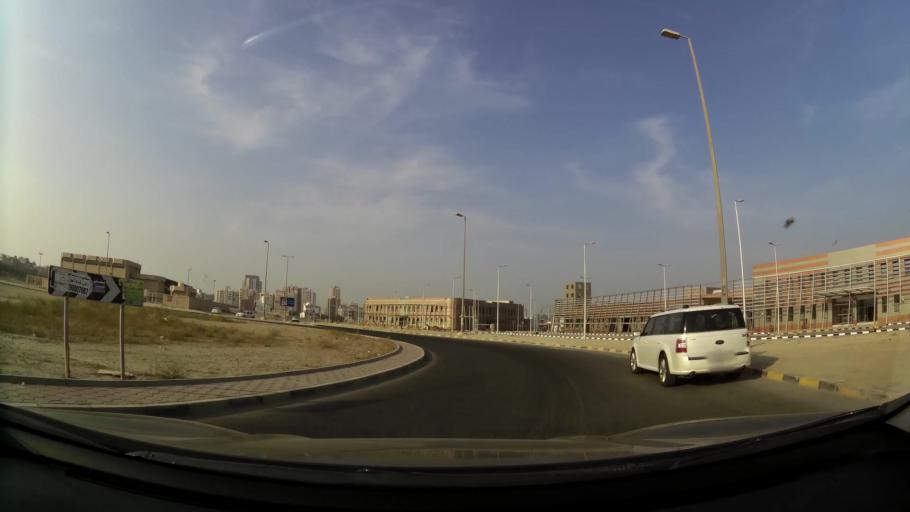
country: KW
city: Al Funaytis
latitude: 29.2413
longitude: 48.0860
